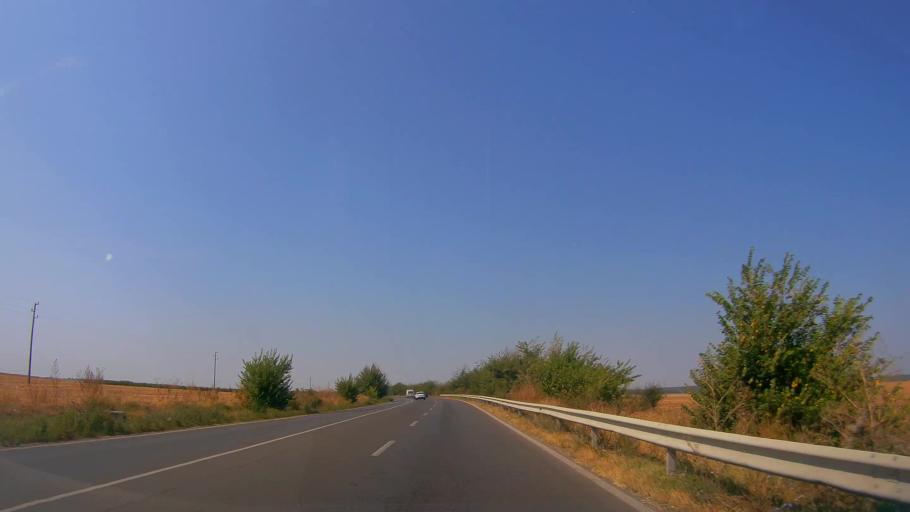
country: BG
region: Ruse
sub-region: Obshtina Vetovo
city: Senovo
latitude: 43.5637
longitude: 26.3406
